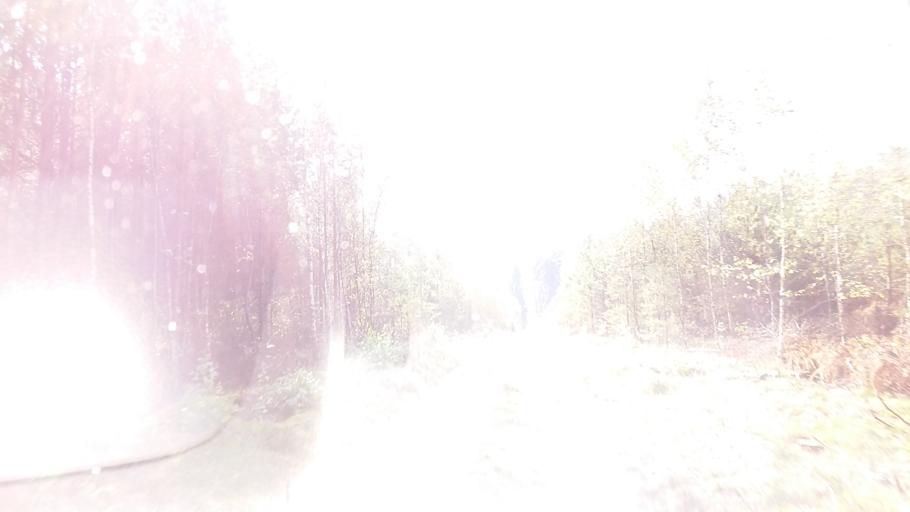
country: PL
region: West Pomeranian Voivodeship
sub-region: Powiat drawski
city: Kalisz Pomorski
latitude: 53.2099
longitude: 15.8966
